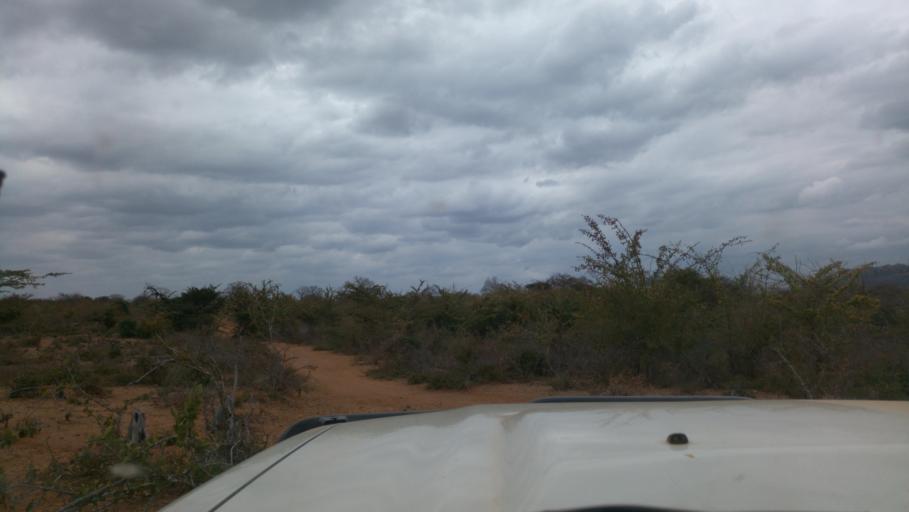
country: KE
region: Makueni
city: Mtito Andei
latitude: -2.0838
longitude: 38.2942
